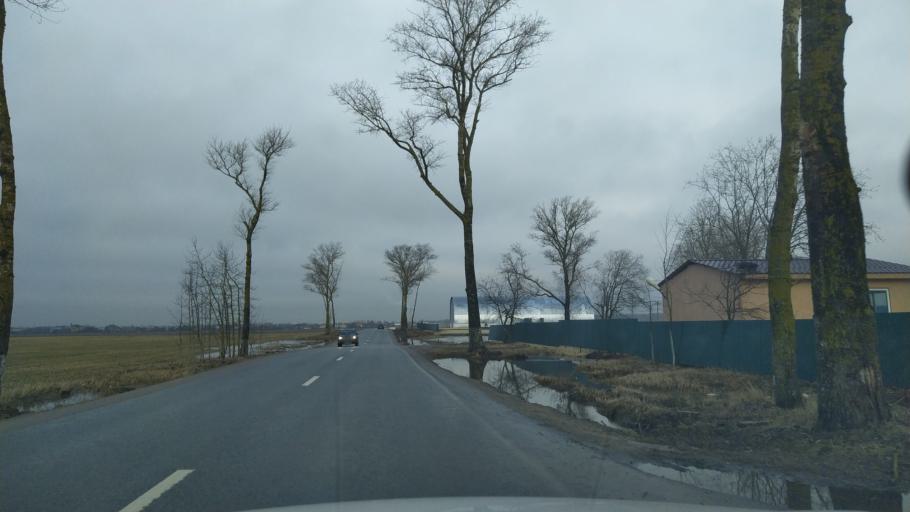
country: RU
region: St.-Petersburg
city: Aleksandrovskaya
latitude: 59.7132
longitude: 30.3326
